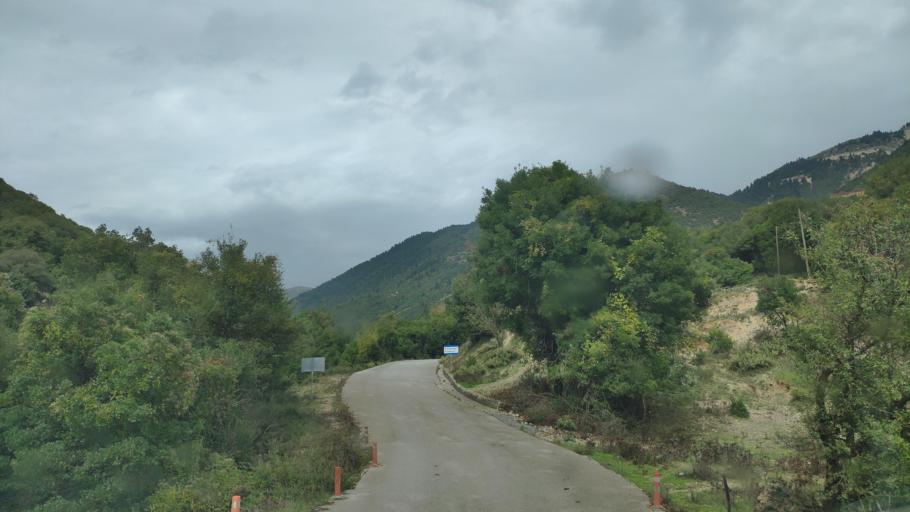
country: GR
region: Epirus
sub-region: Nomos Thesprotias
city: Paramythia
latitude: 39.4306
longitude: 20.6250
